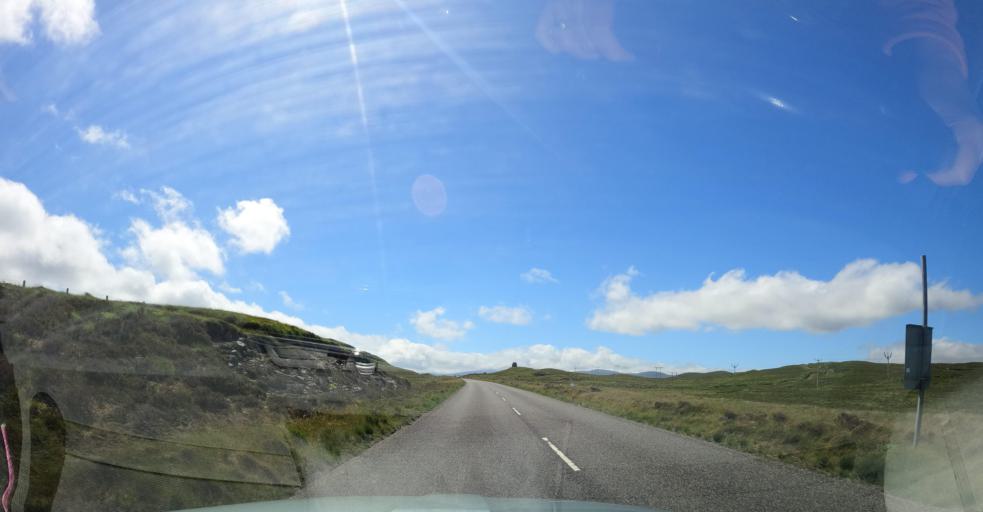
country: GB
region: Scotland
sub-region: Eilean Siar
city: Harris
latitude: 58.0821
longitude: -6.6452
